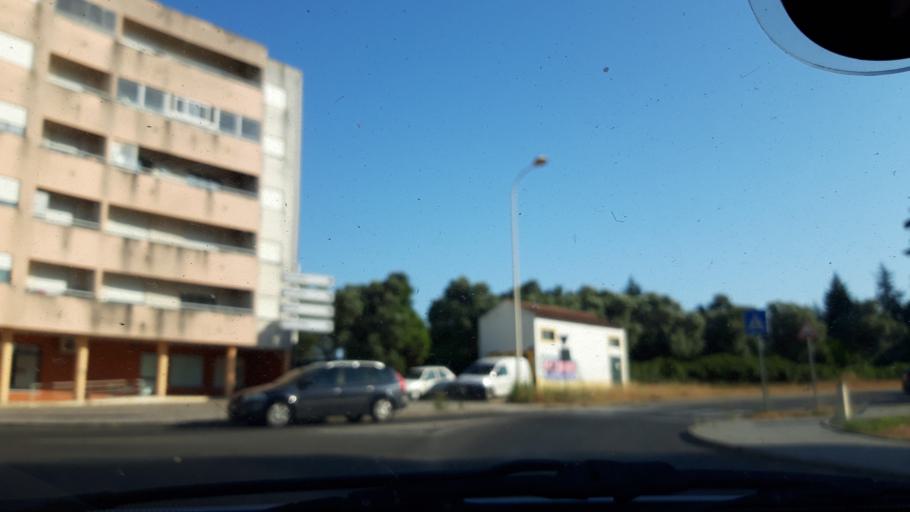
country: PT
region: Santarem
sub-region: Torres Novas
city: Torres Novas
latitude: 39.4766
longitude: -8.5502
